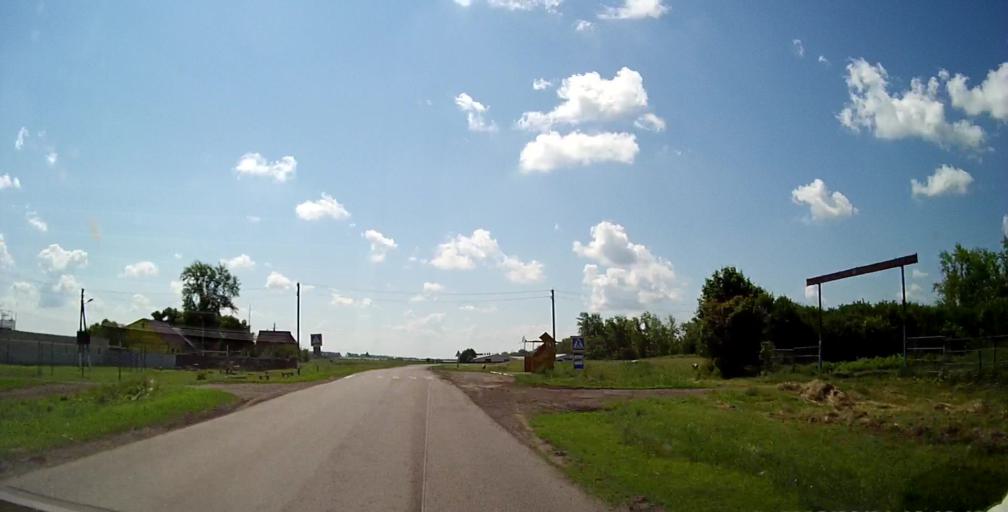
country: RU
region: Lipetsk
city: Chaplygin
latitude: 53.3178
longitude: 39.9589
